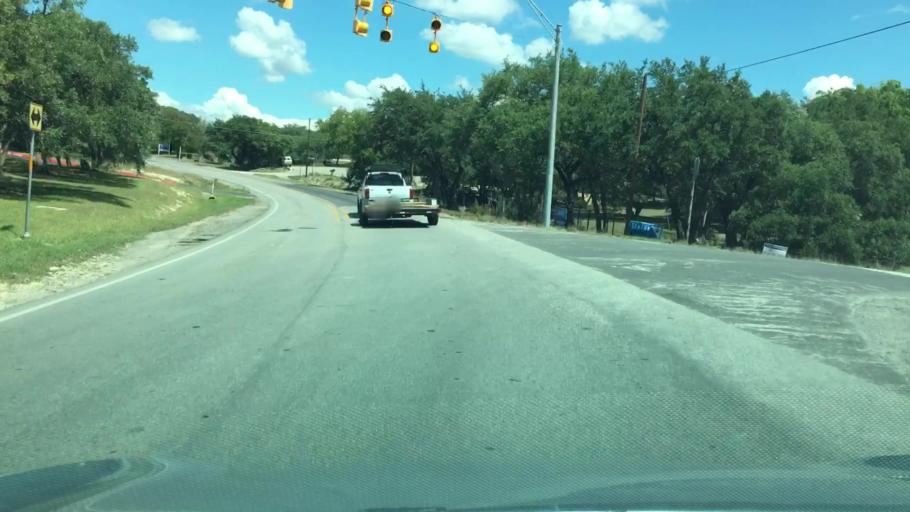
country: US
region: Texas
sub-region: Hays County
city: Wimberley
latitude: 29.9989
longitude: -98.0846
